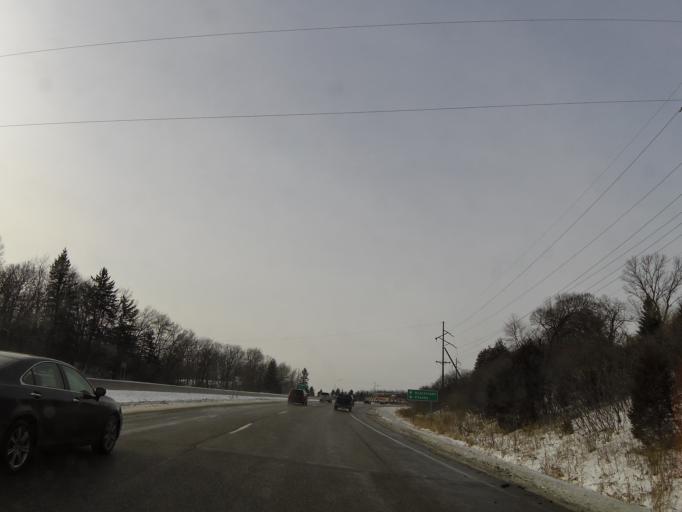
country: US
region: Minnesota
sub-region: Hennepin County
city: Shorewood
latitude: 44.8933
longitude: -93.5769
